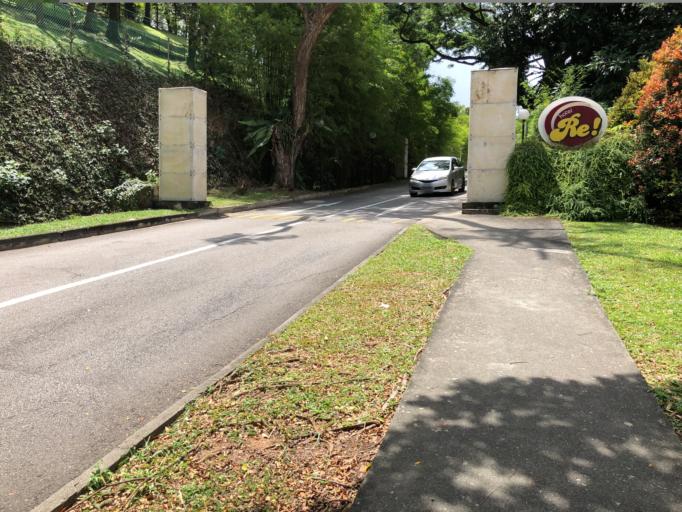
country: SG
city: Singapore
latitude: 1.2858
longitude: 103.8394
